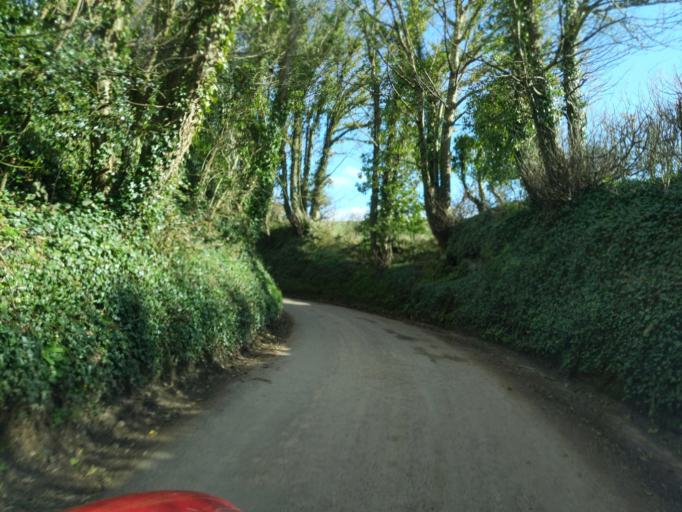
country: GB
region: England
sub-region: Devon
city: Kingsbridge
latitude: 50.2910
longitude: -3.7584
